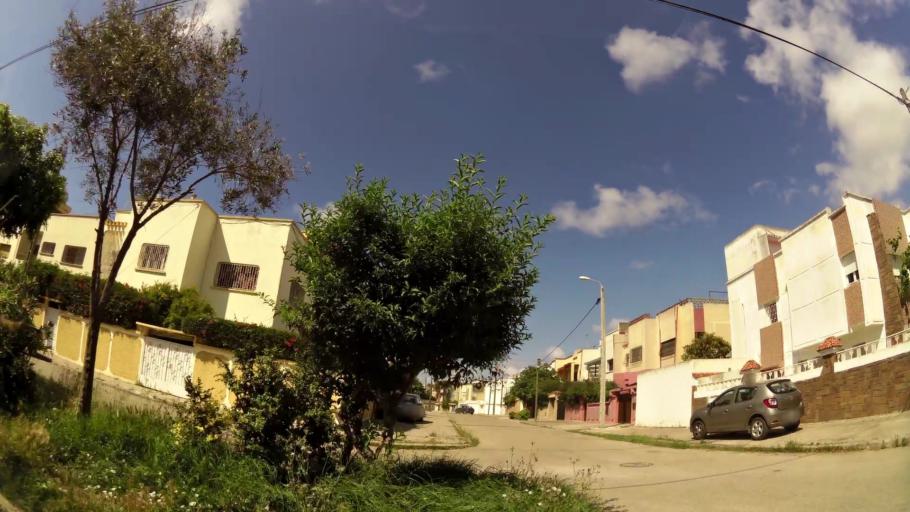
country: MA
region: Rabat-Sale-Zemmour-Zaer
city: Sale
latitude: 34.0380
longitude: -6.7893
